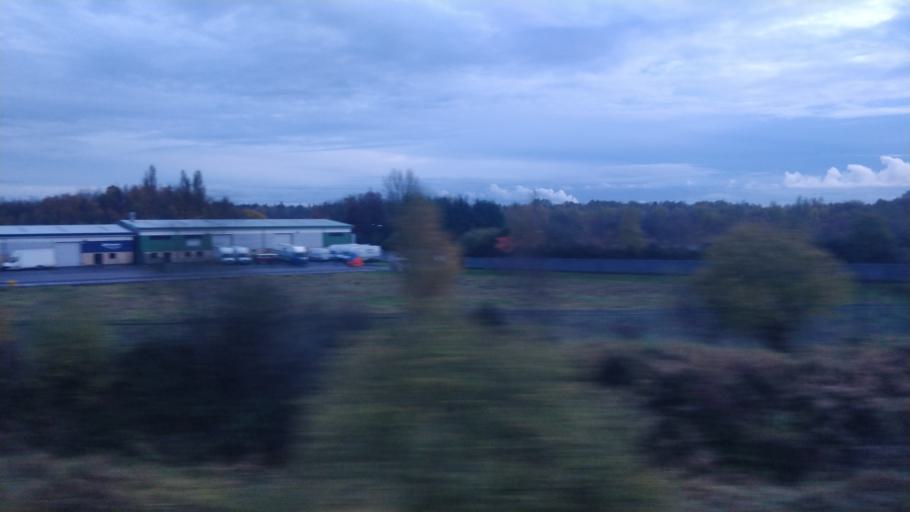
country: GB
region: England
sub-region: Borough of Wigan
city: Ince-in-Makerfield
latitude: 53.5380
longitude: -2.6022
